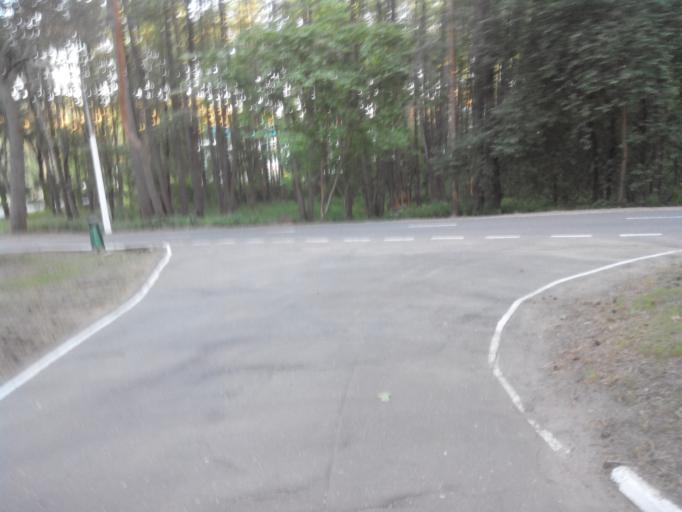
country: BY
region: Minsk
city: Narach
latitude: 54.8383
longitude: 26.7143
